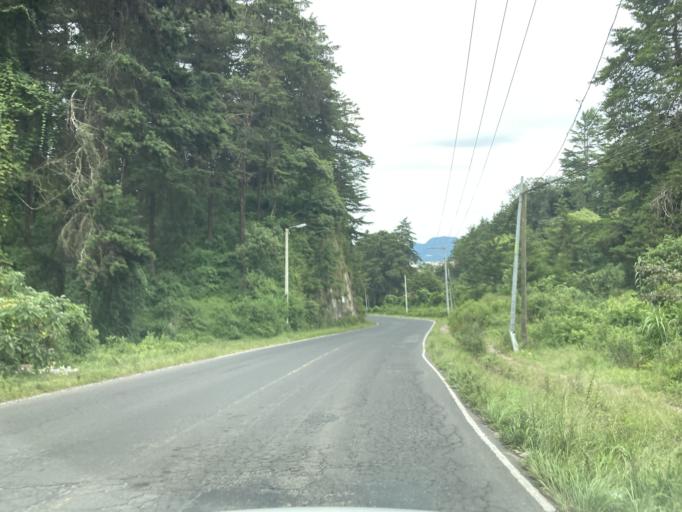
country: GT
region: Guatemala
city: San Jose Pinula
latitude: 14.5346
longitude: -90.4087
